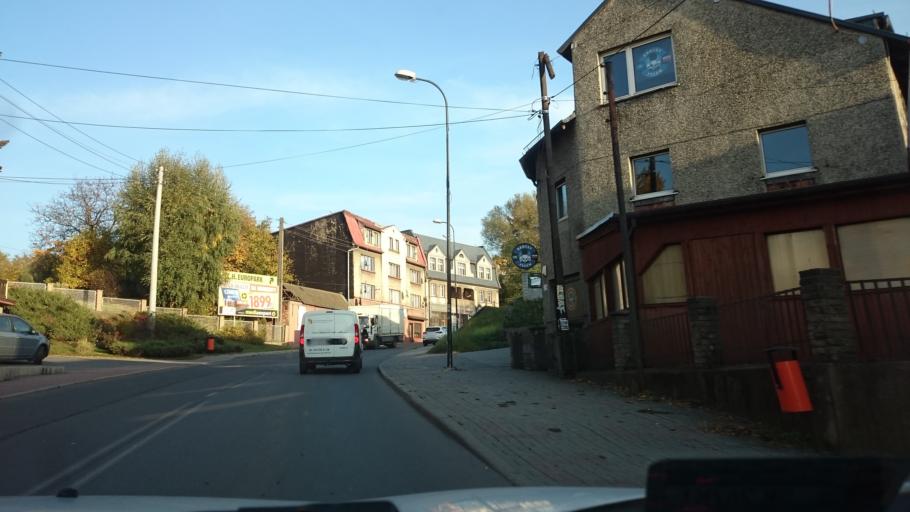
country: PL
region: Silesian Voivodeship
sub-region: Powiat wodzislawski
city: Pszow
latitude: 50.0425
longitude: 18.3946
